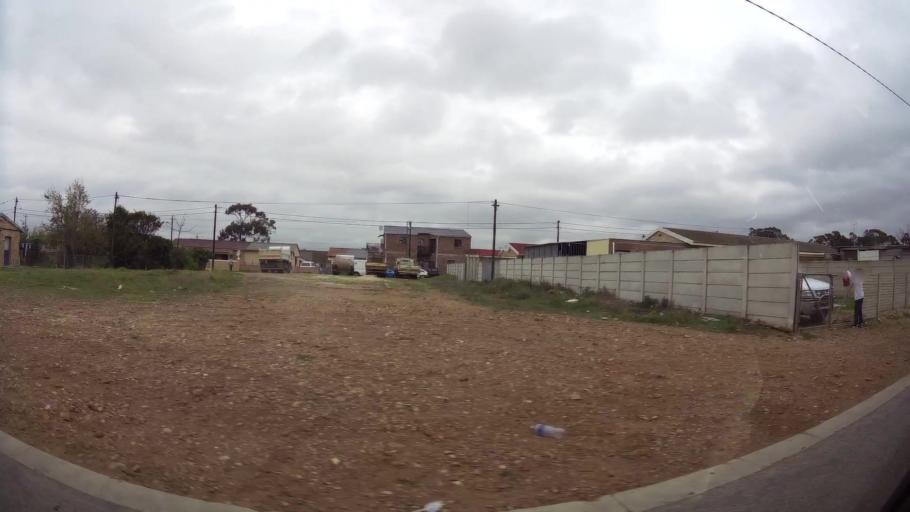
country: ZA
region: Eastern Cape
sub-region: Nelson Mandela Bay Metropolitan Municipality
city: Port Elizabeth
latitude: -33.9025
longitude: 25.5685
